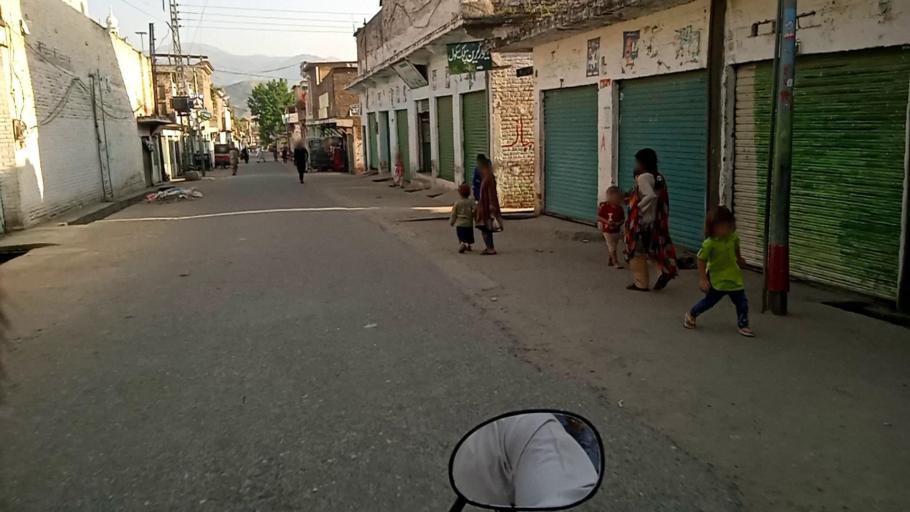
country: PK
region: Khyber Pakhtunkhwa
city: Mingora
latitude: 34.8132
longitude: 72.3594
